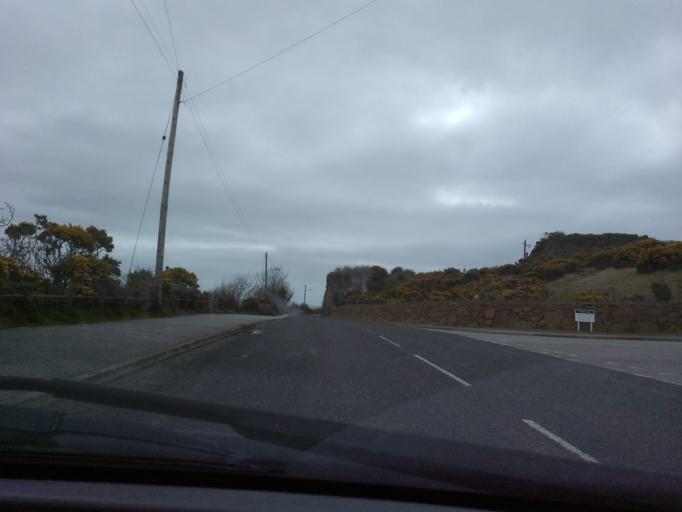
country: GB
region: England
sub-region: Cornwall
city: Penzance
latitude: 50.0983
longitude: -5.5420
